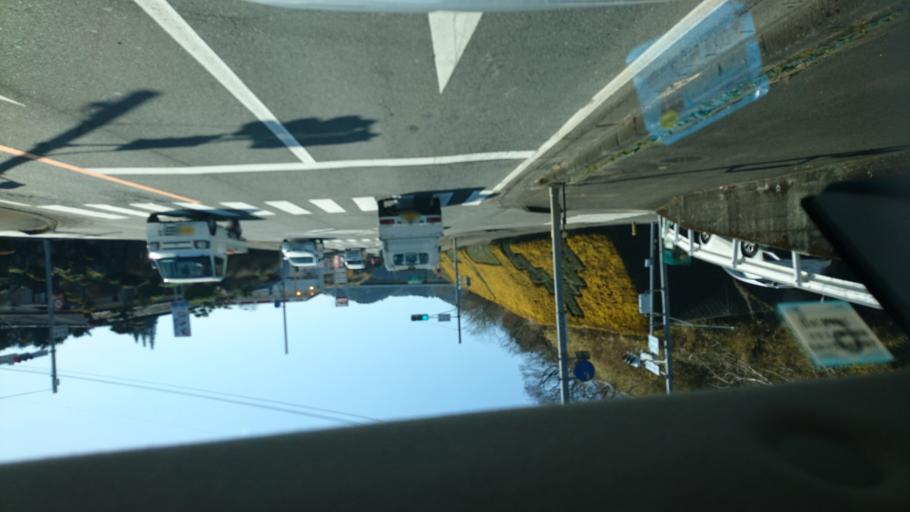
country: JP
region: Oita
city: Takedamachi
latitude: 32.6839
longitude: 131.3497
